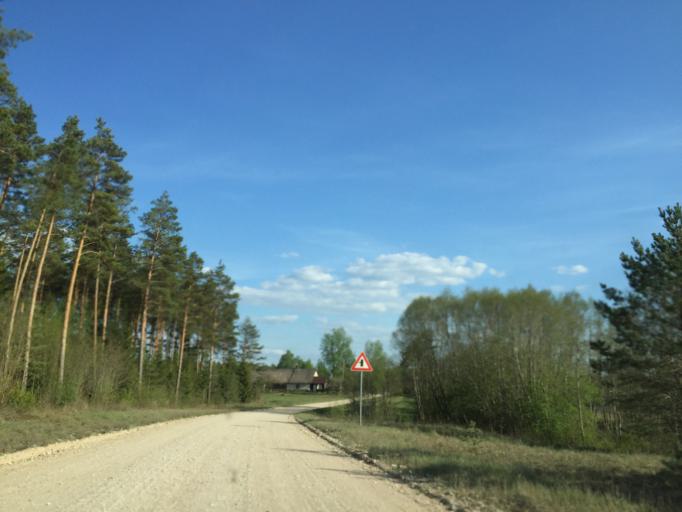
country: LV
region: Pargaujas
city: Stalbe
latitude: 57.3724
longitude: 24.9856
